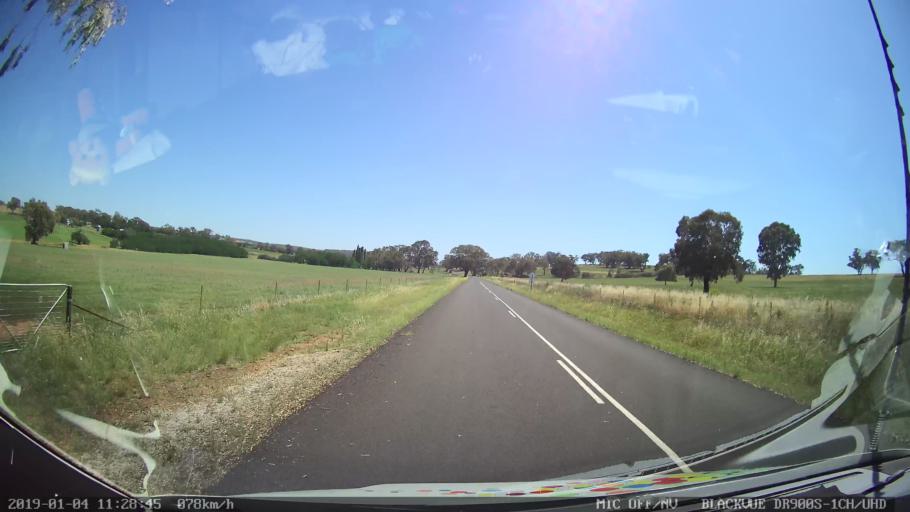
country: AU
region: New South Wales
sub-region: Cabonne
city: Molong
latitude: -33.0962
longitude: 148.7723
